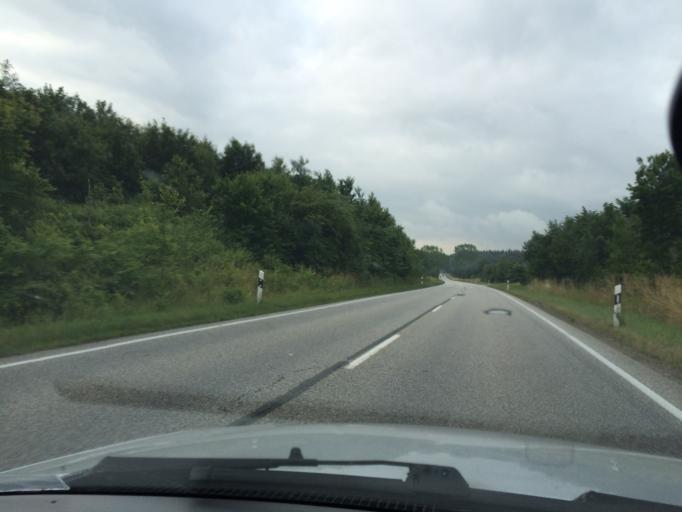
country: DE
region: Schleswig-Holstein
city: Oeversee
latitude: 54.6836
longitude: 9.4338
